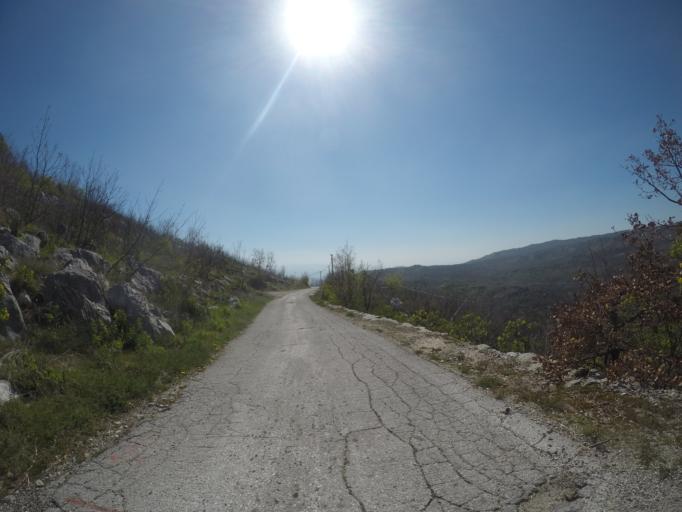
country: ME
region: Danilovgrad
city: Danilovgrad
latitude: 42.5320
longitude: 19.0205
